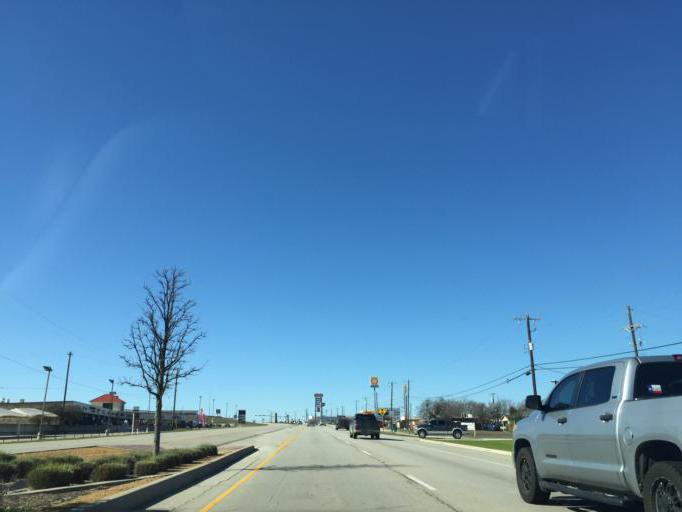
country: US
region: Texas
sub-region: Parker County
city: Hudson Oaks
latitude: 32.7552
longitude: -97.6936
